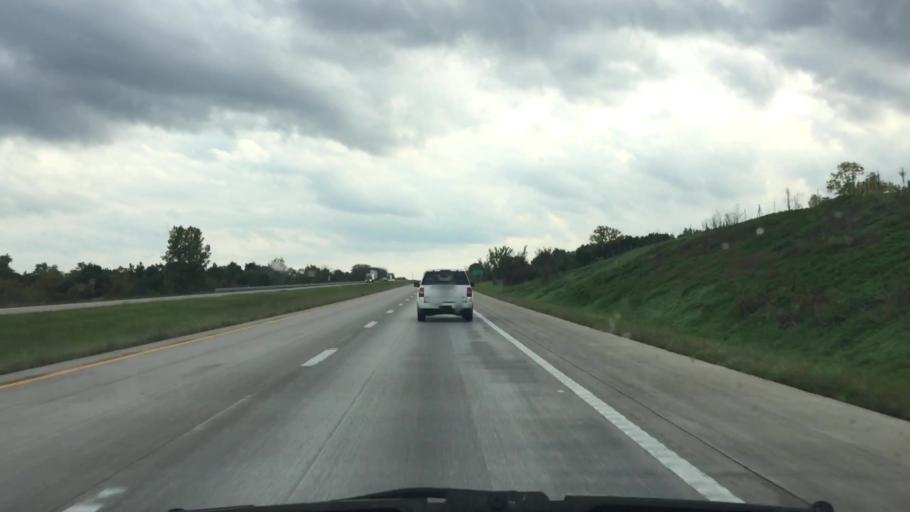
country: US
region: Missouri
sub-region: Clinton County
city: Cameron
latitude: 39.6559
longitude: -94.2389
